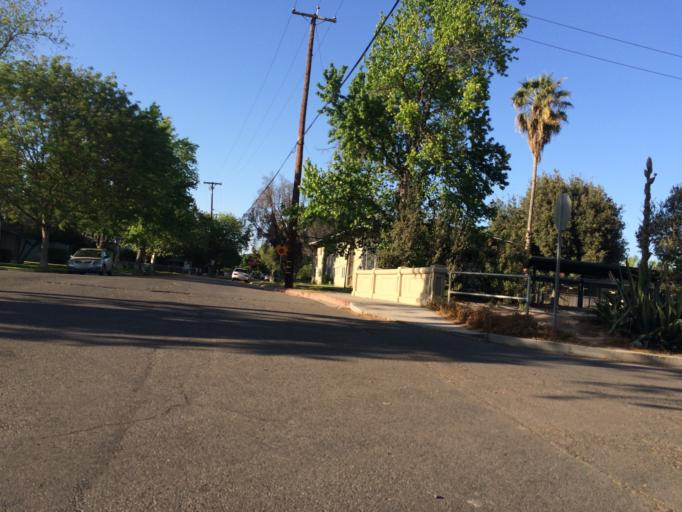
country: US
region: California
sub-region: Fresno County
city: Fresno
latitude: 36.7544
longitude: -119.7976
